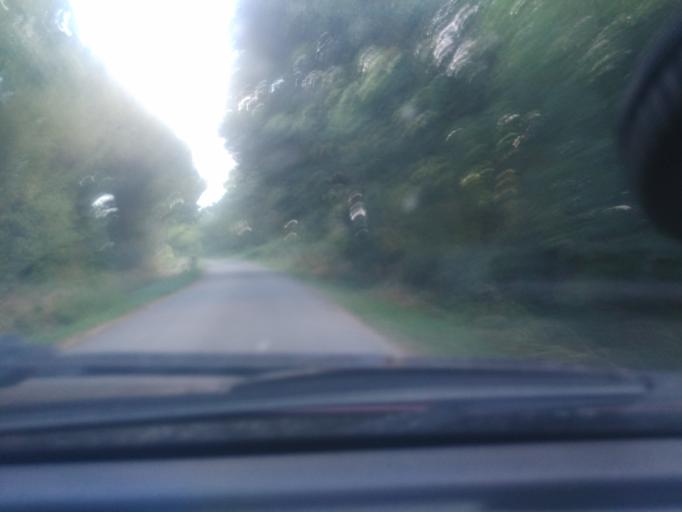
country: FR
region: Pays de la Loire
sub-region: Departement de la Vendee
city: La Ferriere
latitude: 46.7108
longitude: -1.3005
